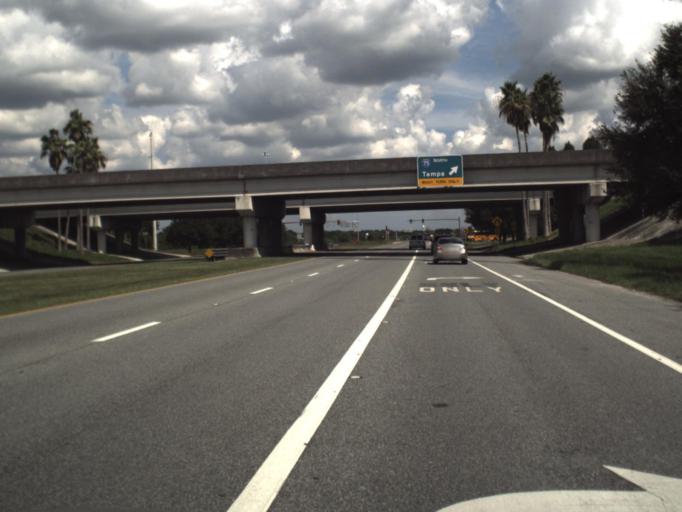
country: US
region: Florida
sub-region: Sarasota County
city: Fruitville
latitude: 27.3382
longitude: -82.4479
